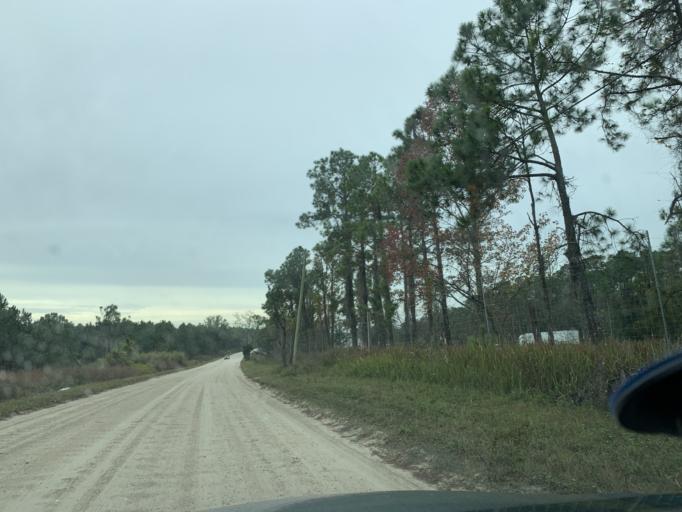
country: US
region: Florida
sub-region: Pasco County
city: Wesley Chapel
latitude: 28.2782
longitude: -82.3257
